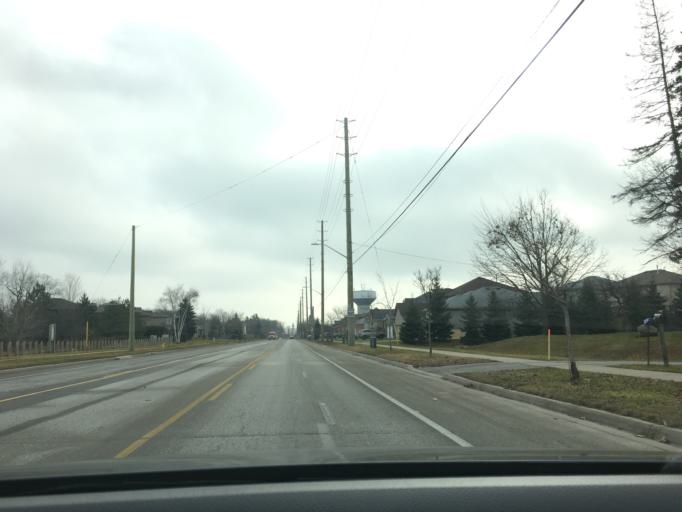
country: CA
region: Ontario
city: Barrie
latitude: 44.3959
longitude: -79.7374
